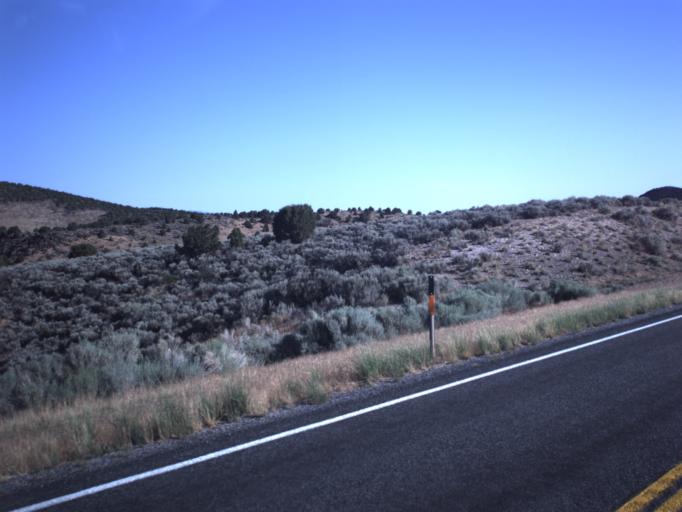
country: US
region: Utah
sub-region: Iron County
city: Parowan
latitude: 38.1036
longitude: -112.9482
